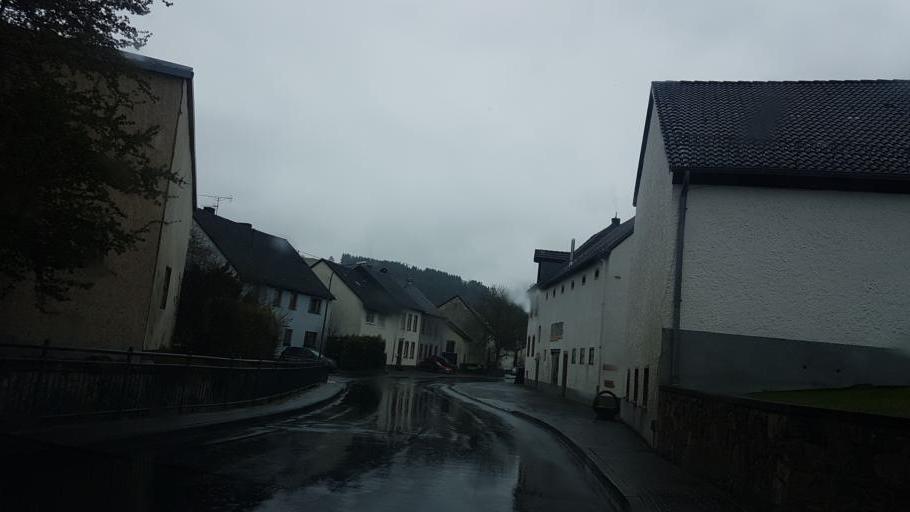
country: DE
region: Rheinland-Pfalz
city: Rockeskyll
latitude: 50.2558
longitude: 6.6944
